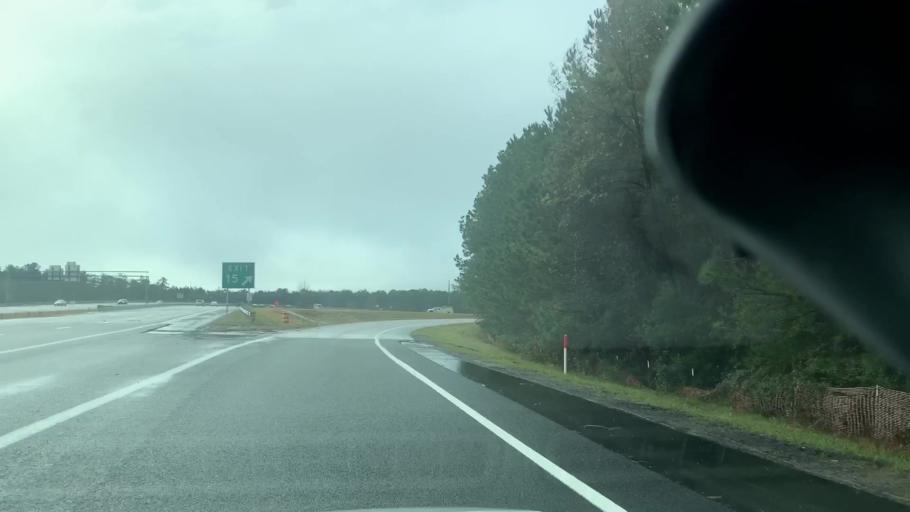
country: US
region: South Carolina
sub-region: Richland County
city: Woodfield
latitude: 34.0550
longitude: -80.9231
